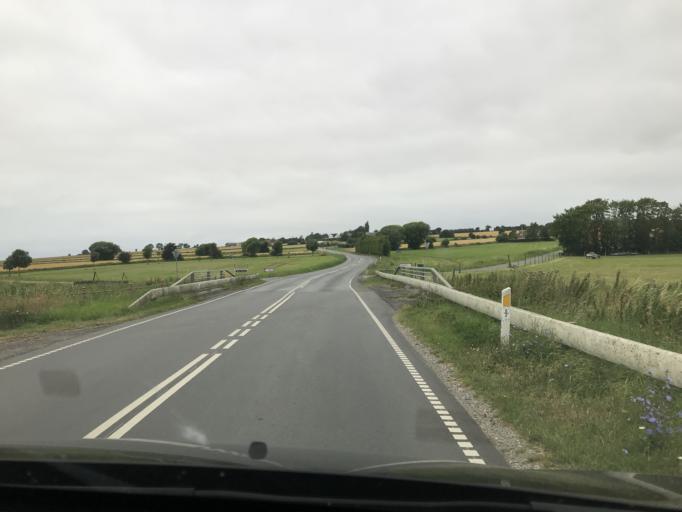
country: DK
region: South Denmark
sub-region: AEro Kommune
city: AEroskobing
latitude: 54.8407
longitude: 10.4392
